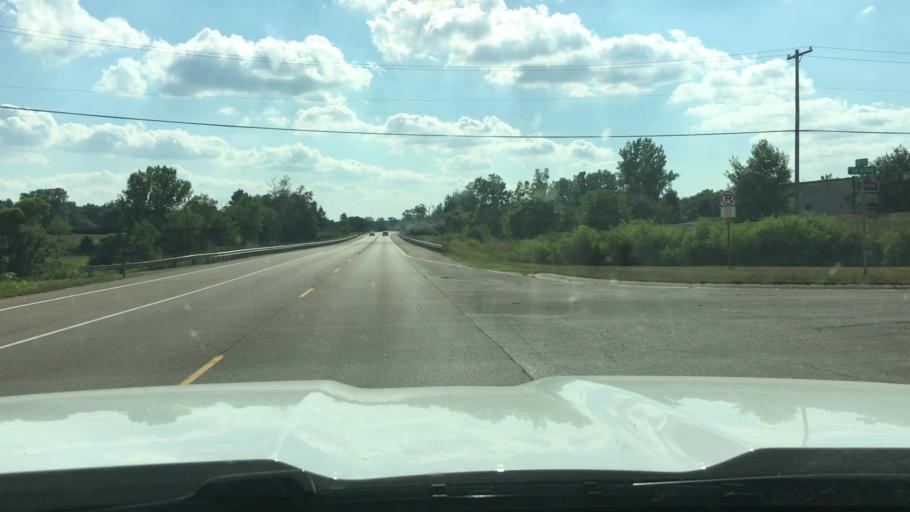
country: US
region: Michigan
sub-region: Ionia County
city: Belding
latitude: 43.0829
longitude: -85.3674
